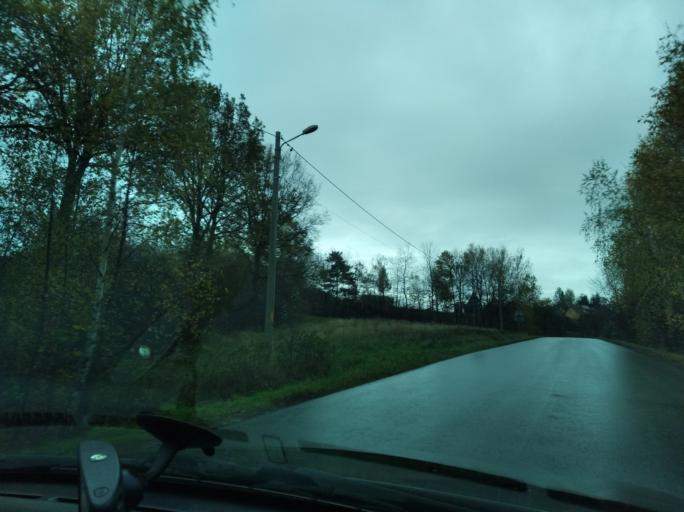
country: PL
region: Subcarpathian Voivodeship
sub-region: Powiat rzeszowski
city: Lecka
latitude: 49.9164
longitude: 22.0286
